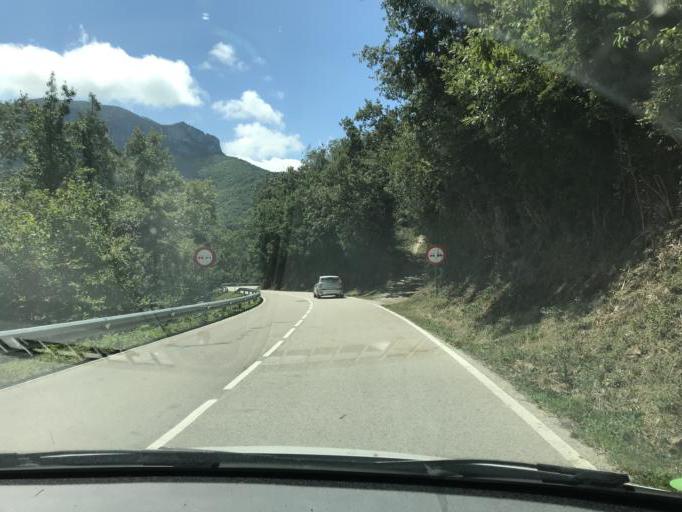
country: ES
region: Cantabria
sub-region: Provincia de Cantabria
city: Cabezon de Liebana
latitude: 43.0758
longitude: -4.4851
